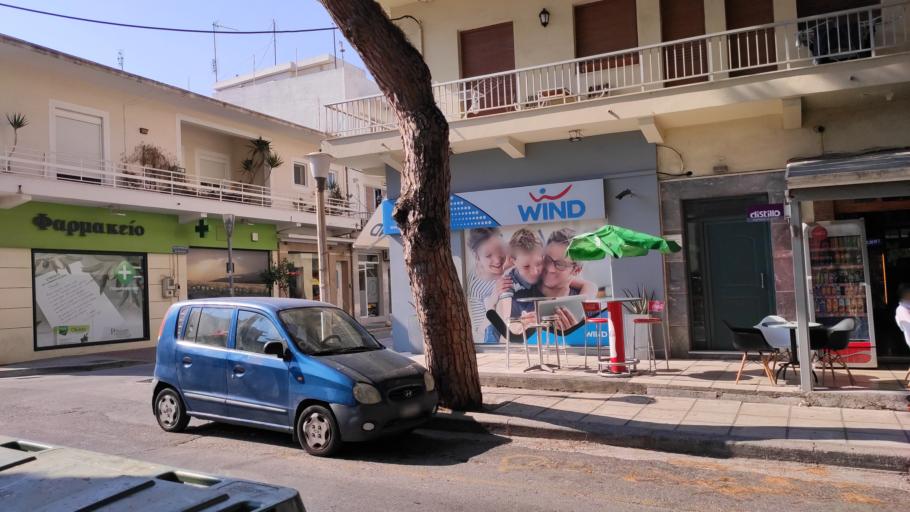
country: GR
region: South Aegean
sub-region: Nomos Dodekanisou
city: Kos
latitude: 36.8920
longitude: 27.2912
